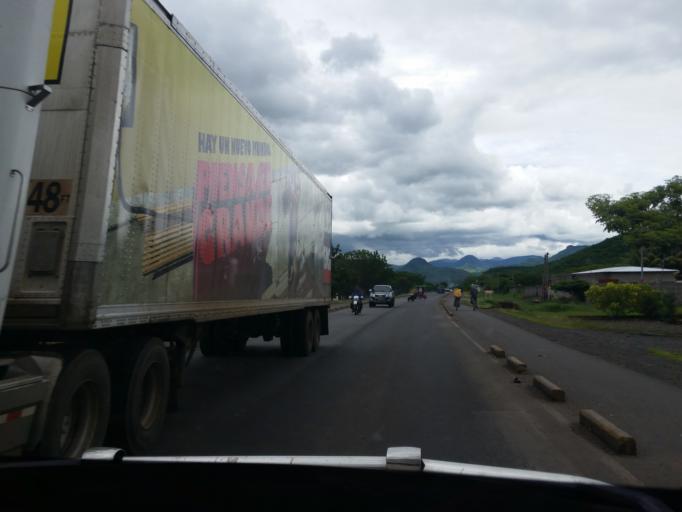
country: NI
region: Matagalpa
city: Ciudad Dario
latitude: 12.8627
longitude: -86.0938
